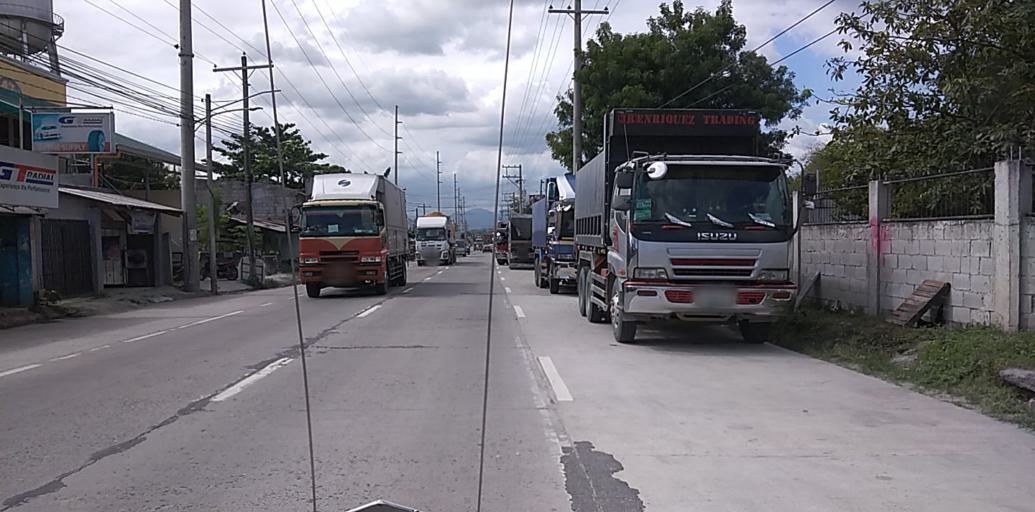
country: PH
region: Central Luzon
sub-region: Province of Pampanga
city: Pio
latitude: 15.0485
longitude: 120.5290
